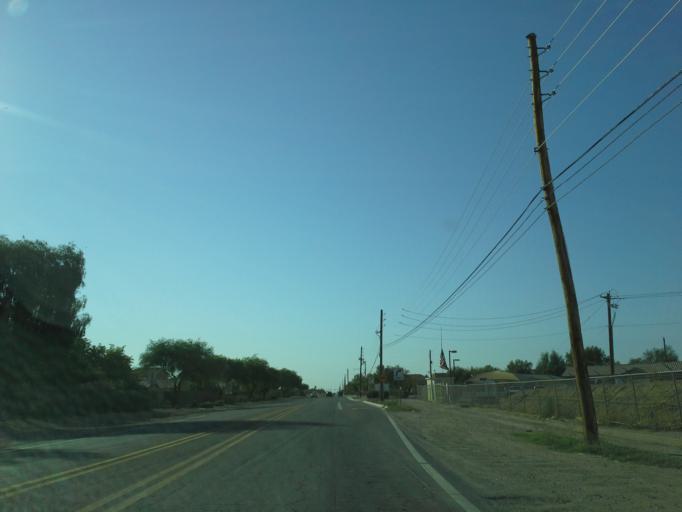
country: US
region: Arizona
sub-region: Pinal County
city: San Tan Valley
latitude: 33.1539
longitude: -111.5566
